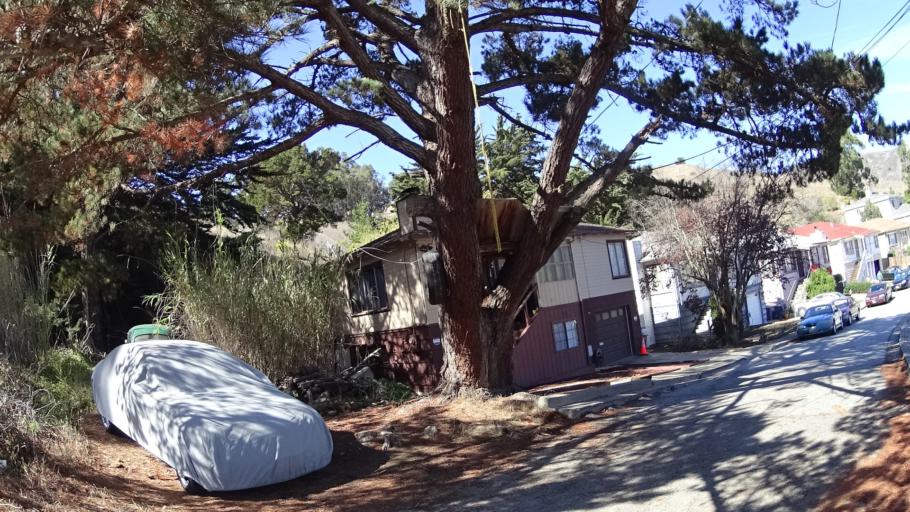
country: US
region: California
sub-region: San Mateo County
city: South San Francisco
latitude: 37.6626
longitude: -122.4137
